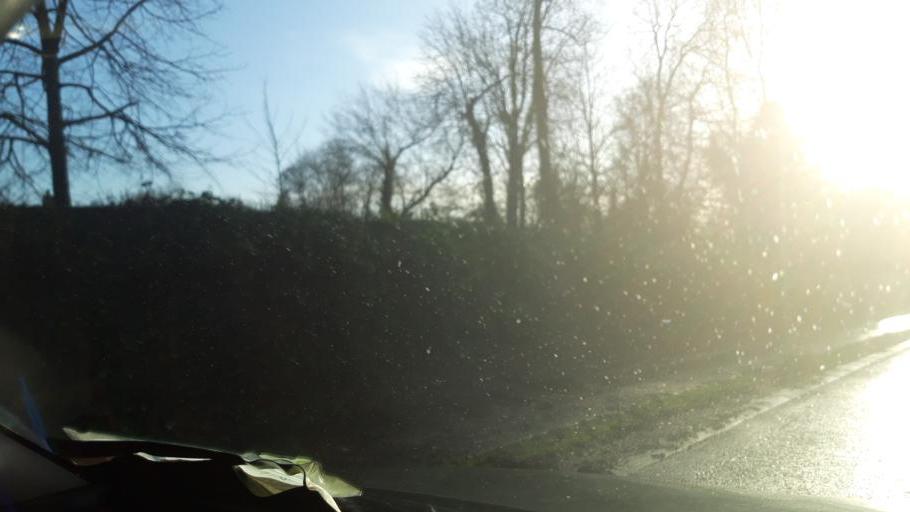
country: GB
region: Northern Ireland
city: Maghera
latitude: 54.8413
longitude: -6.6760
